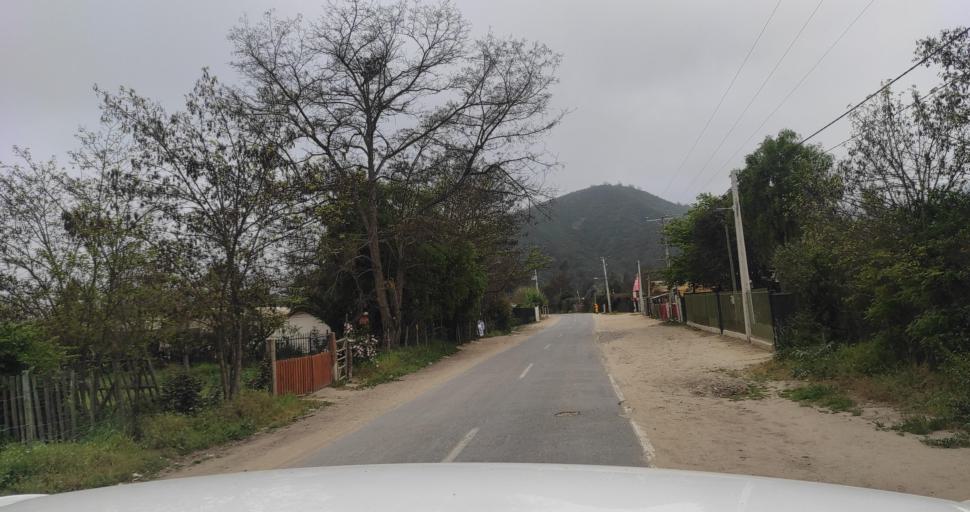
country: CL
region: Valparaiso
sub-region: Provincia de Marga Marga
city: Villa Alemana
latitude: -33.3606
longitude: -71.3019
